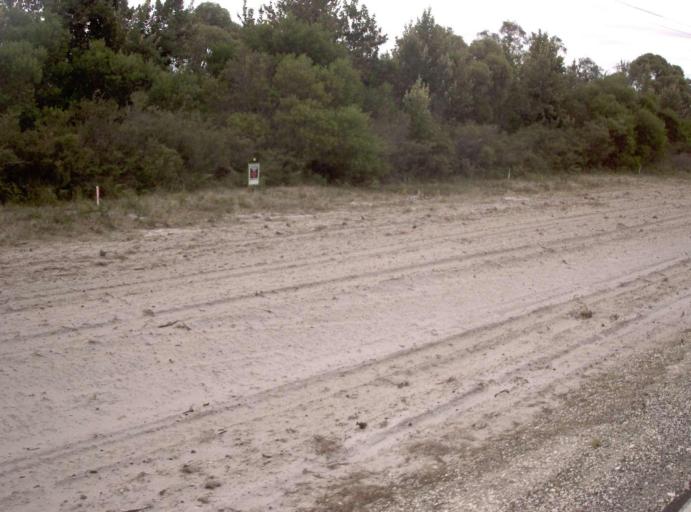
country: AU
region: Victoria
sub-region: East Gippsland
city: Bairnsdale
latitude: -38.0952
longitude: 147.5129
